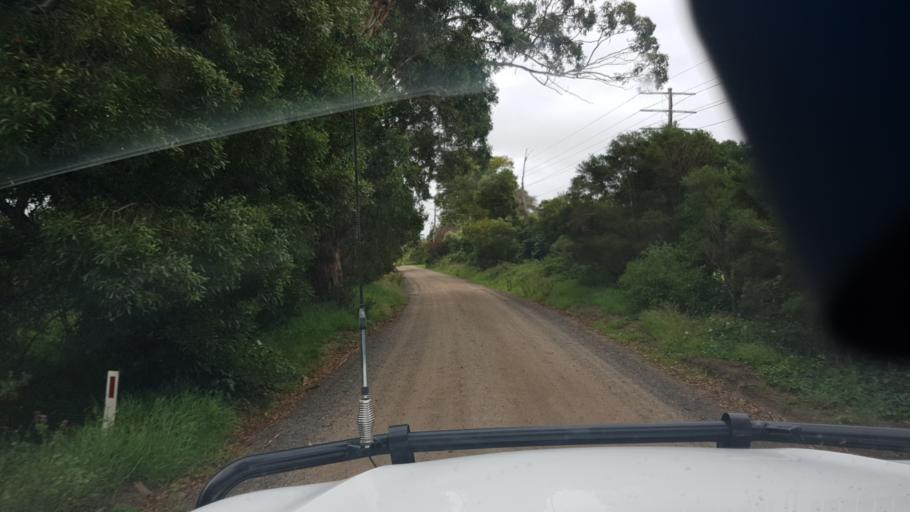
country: AU
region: Victoria
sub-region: Cardinia
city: Bunyip
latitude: -38.1007
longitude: 145.7440
